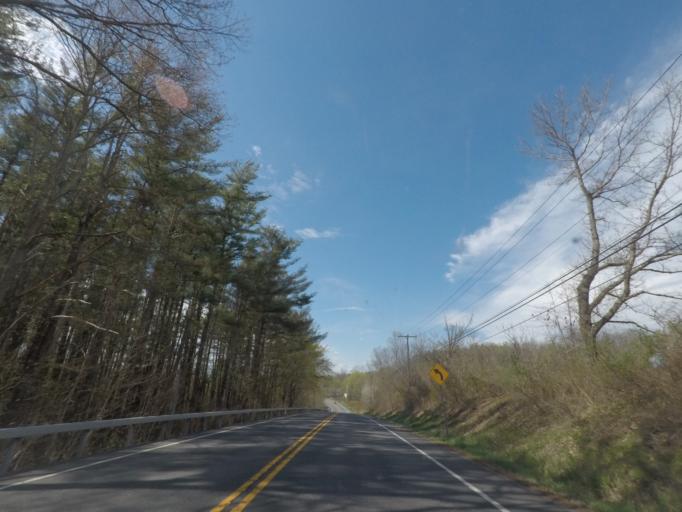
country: US
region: New York
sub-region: Greene County
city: Cairo
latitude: 42.3334
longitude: -74.0202
